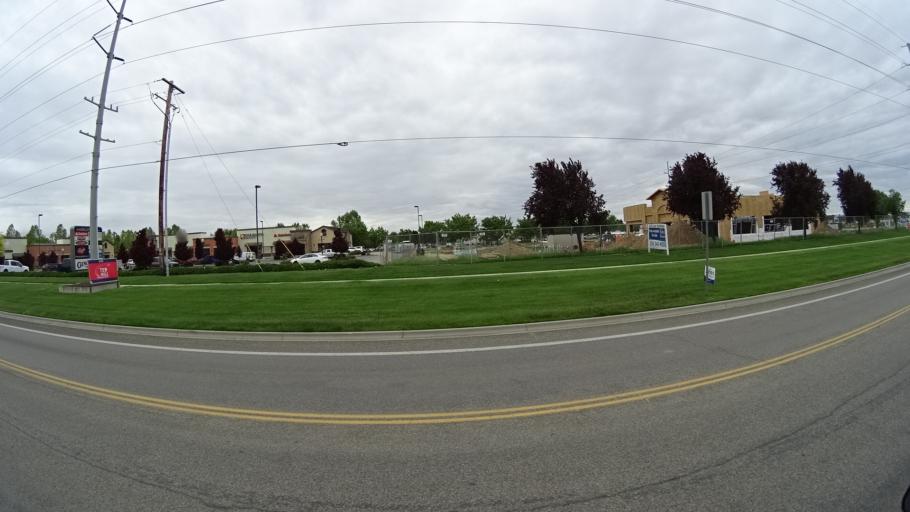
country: US
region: Idaho
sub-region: Ada County
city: Meridian
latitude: 43.6480
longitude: -116.4318
